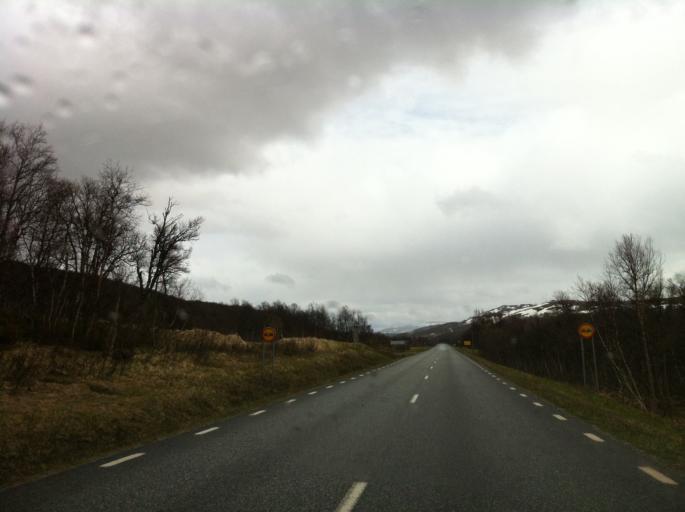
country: NO
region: Sor-Trondelag
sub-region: Tydal
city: Aas
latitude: 62.5915
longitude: 12.1903
